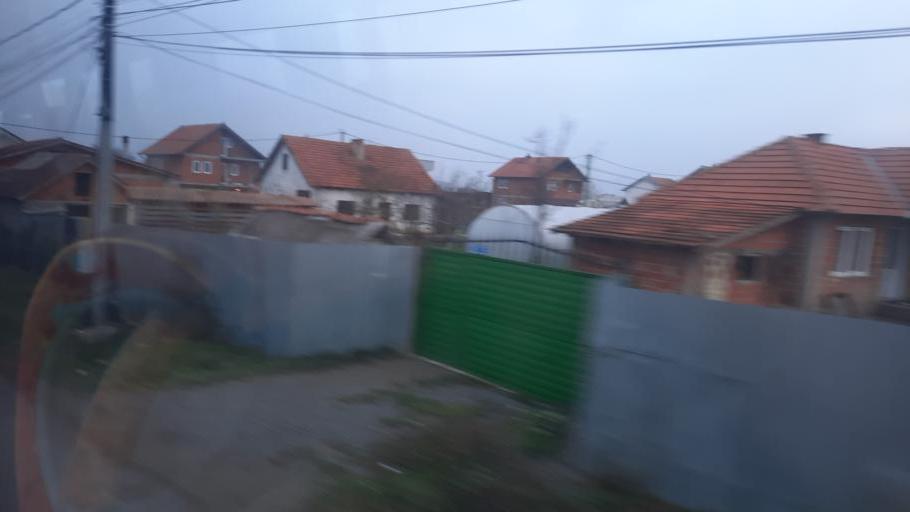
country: XK
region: Pristina
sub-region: Komuna e Drenasit
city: Glogovac
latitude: 42.6011
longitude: 20.8977
